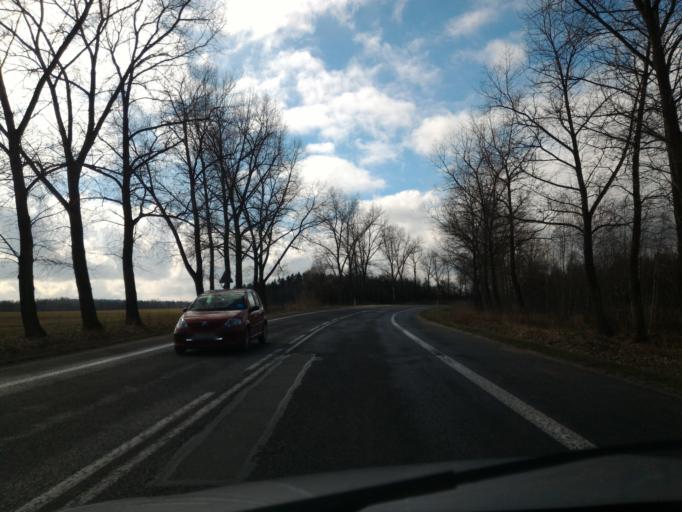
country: PL
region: Lower Silesian Voivodeship
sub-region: Powiat zgorzelecki
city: Sulikow
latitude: 51.0659
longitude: 15.0027
